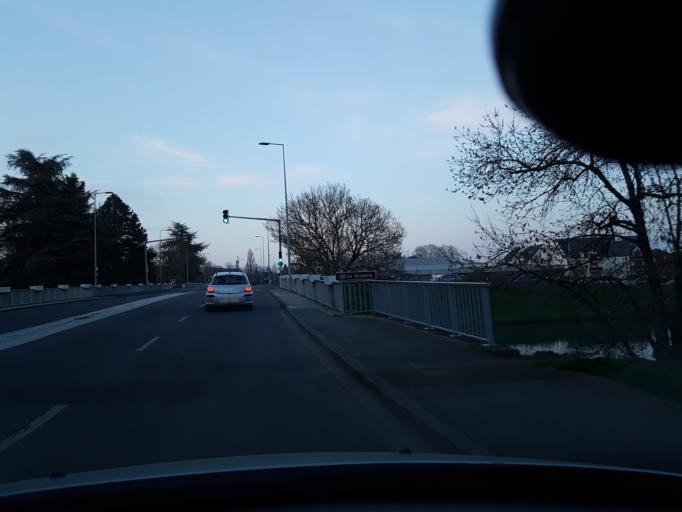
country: FR
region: Centre
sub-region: Departement du Cher
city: Bourges
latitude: 47.0908
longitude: 2.3987
